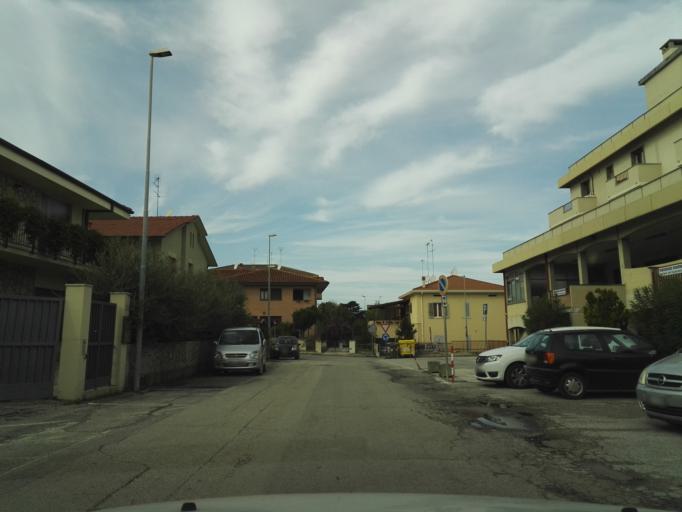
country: IT
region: The Marches
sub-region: Provincia di Pesaro e Urbino
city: Marotta
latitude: 43.7677
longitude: 13.1386
